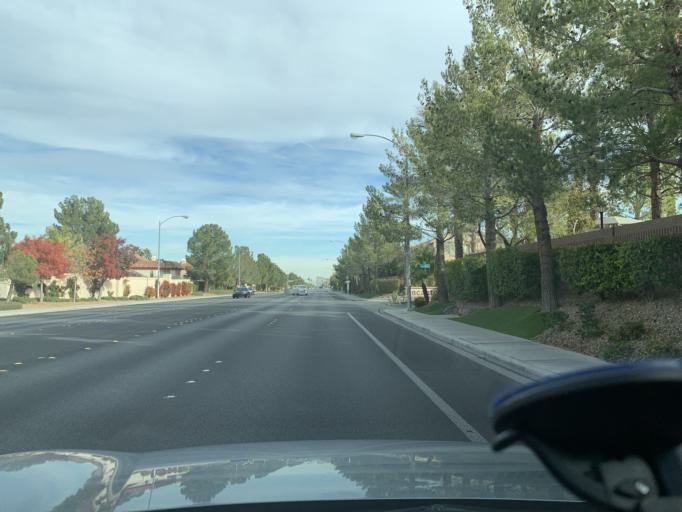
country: US
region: Nevada
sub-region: Clark County
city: Spring Valley
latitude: 36.0923
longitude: -115.2466
